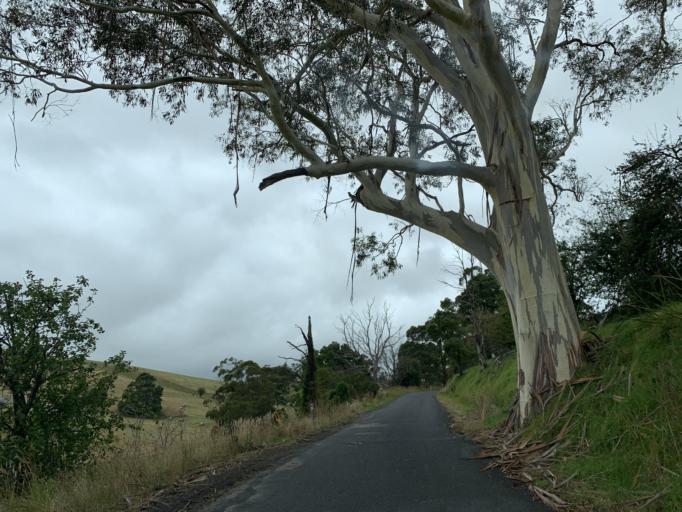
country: AU
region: Victoria
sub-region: Baw Baw
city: Warragul
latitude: -38.2929
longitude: 145.8626
